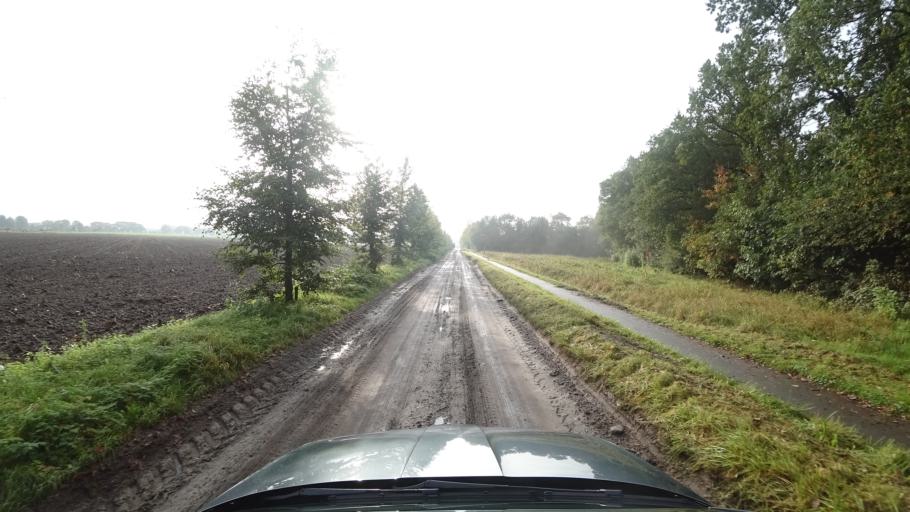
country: NL
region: Gelderland
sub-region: Gemeente Renkum
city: Renkum
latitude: 51.9928
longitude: 5.7390
